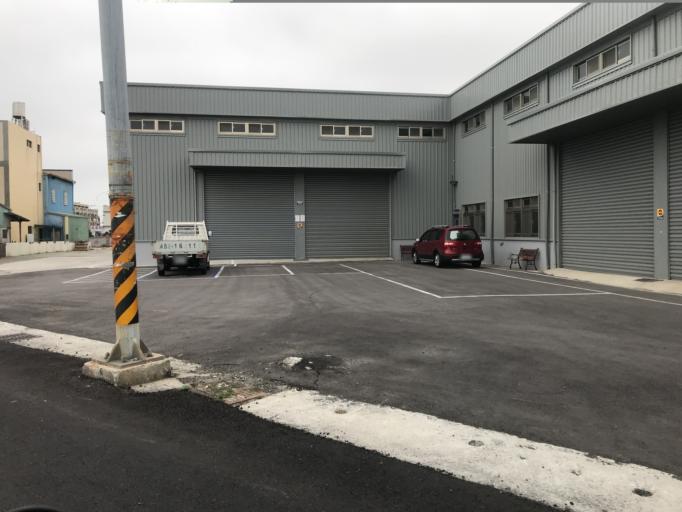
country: TW
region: Taiwan
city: Fengyuan
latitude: 24.3697
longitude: 120.6014
